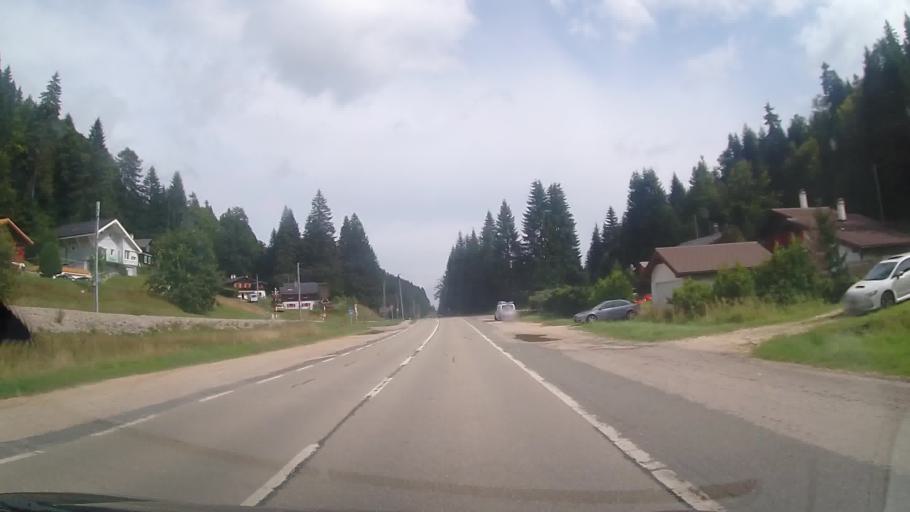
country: CH
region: Vaud
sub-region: Nyon District
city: Saint-Cergue
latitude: 46.4531
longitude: 6.1203
